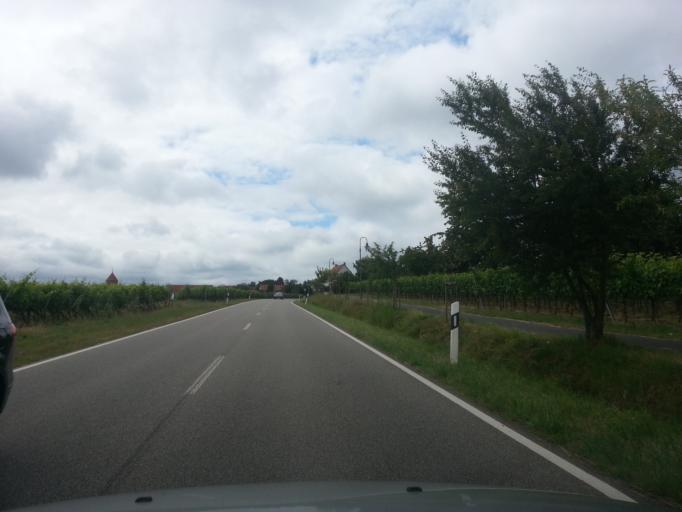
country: DE
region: Rheinland-Pfalz
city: Weisenheim am Berg
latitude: 49.5182
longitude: 8.1519
